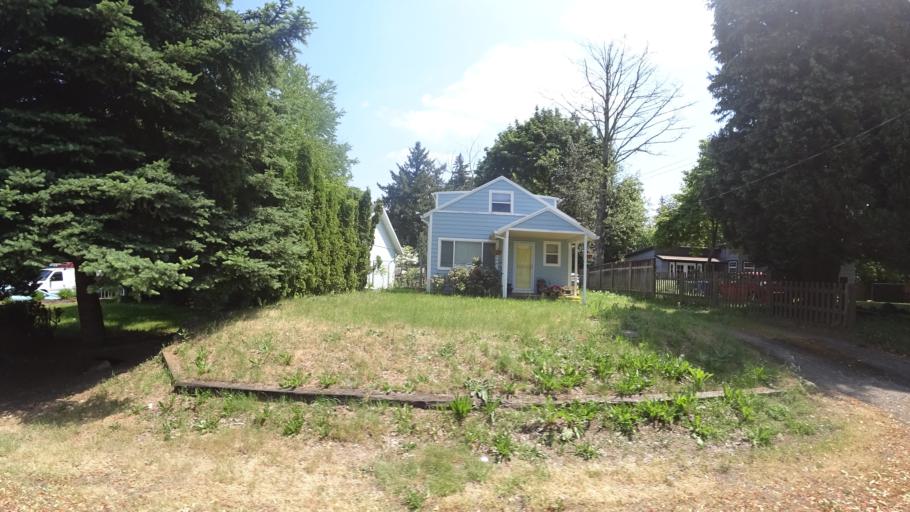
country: US
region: Oregon
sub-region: Multnomah County
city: Fairview
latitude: 45.5319
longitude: -122.5036
